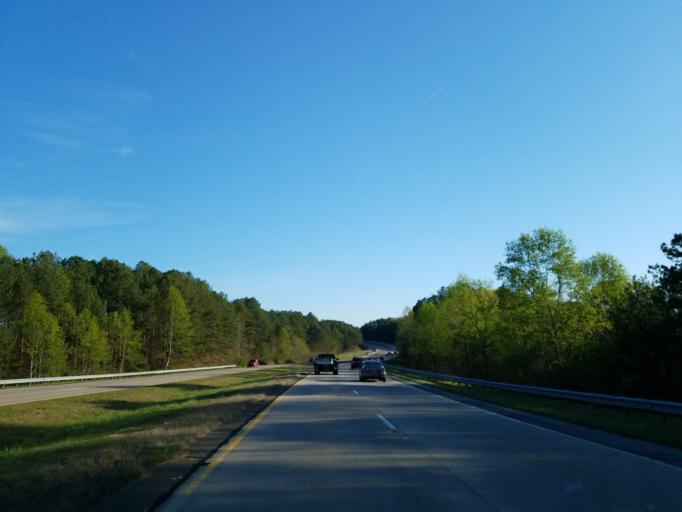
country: US
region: Georgia
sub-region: Gilmer County
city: Ellijay
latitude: 34.5697
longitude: -84.5205
